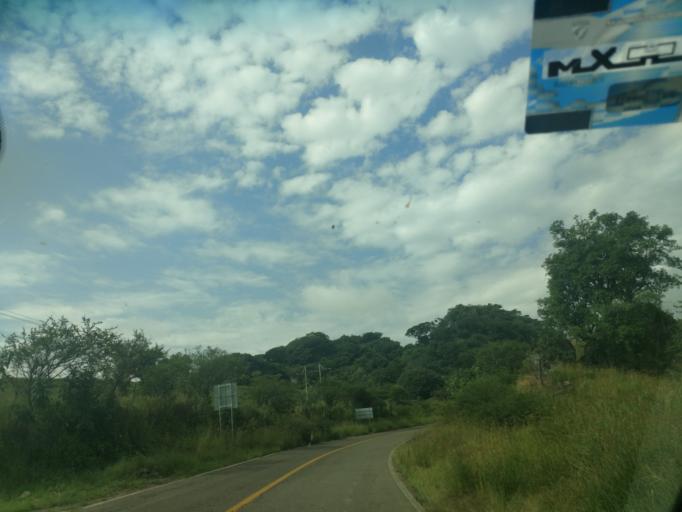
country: MX
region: Jalisco
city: El Salto
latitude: 20.4175
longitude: -104.5007
